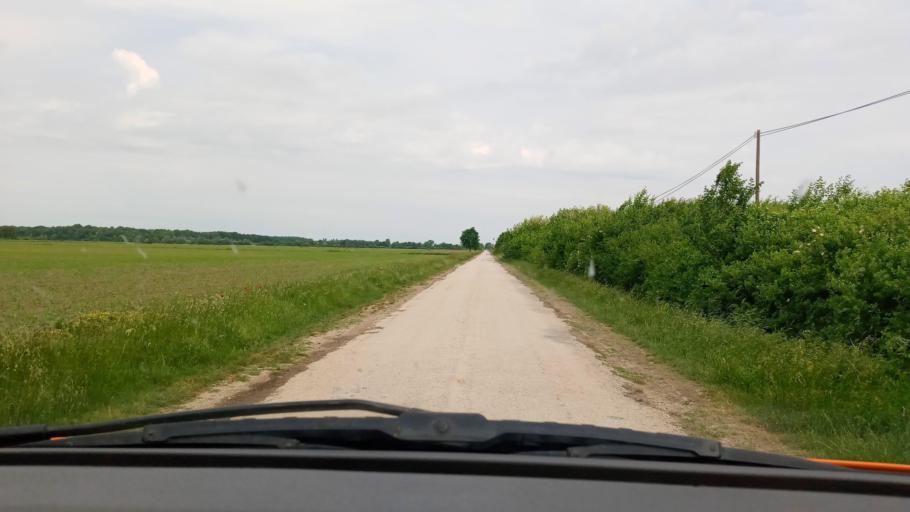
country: HU
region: Baranya
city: Vajszlo
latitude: 45.9120
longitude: 18.0272
